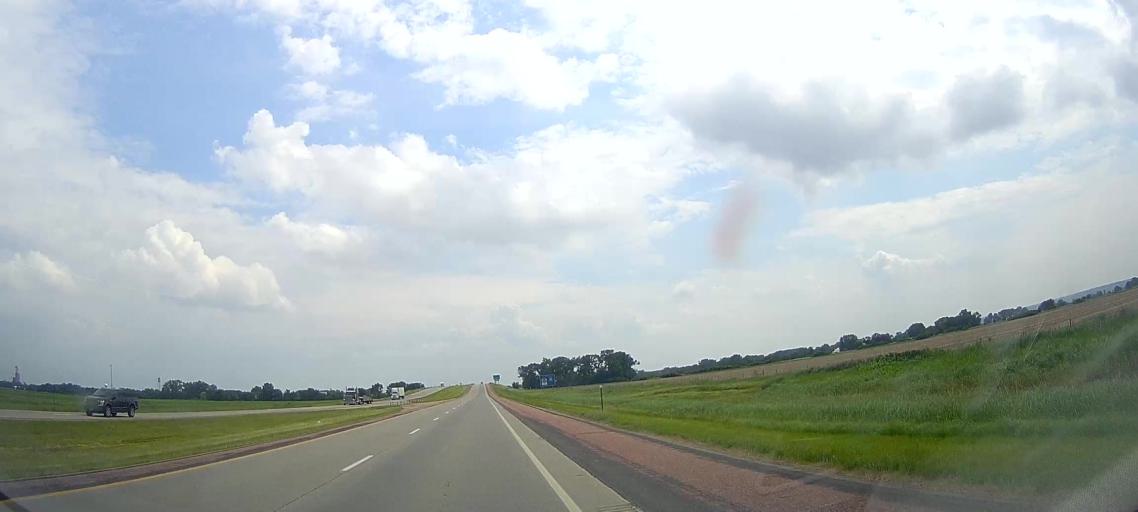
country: US
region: South Dakota
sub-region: Union County
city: Elk Point
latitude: 42.6997
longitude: -96.6974
